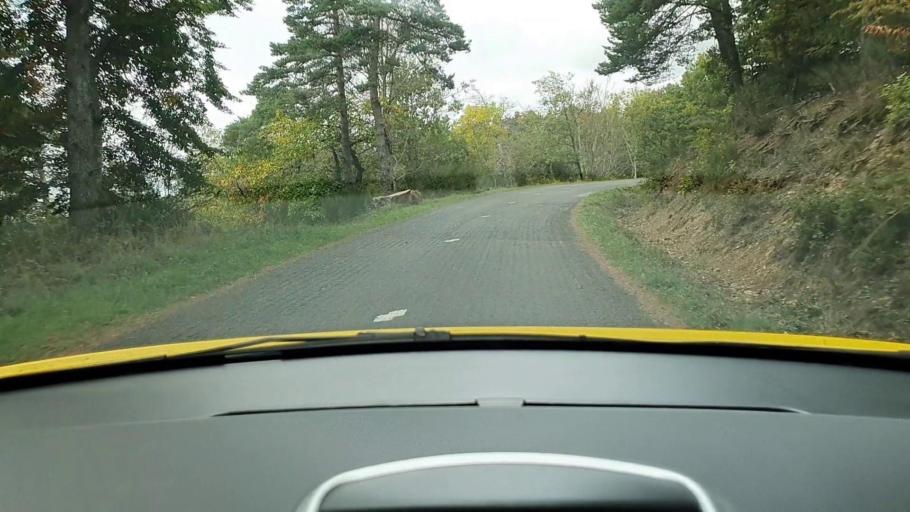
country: FR
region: Languedoc-Roussillon
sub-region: Departement de la Lozere
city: Meyrueis
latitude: 44.0773
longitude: 3.4149
